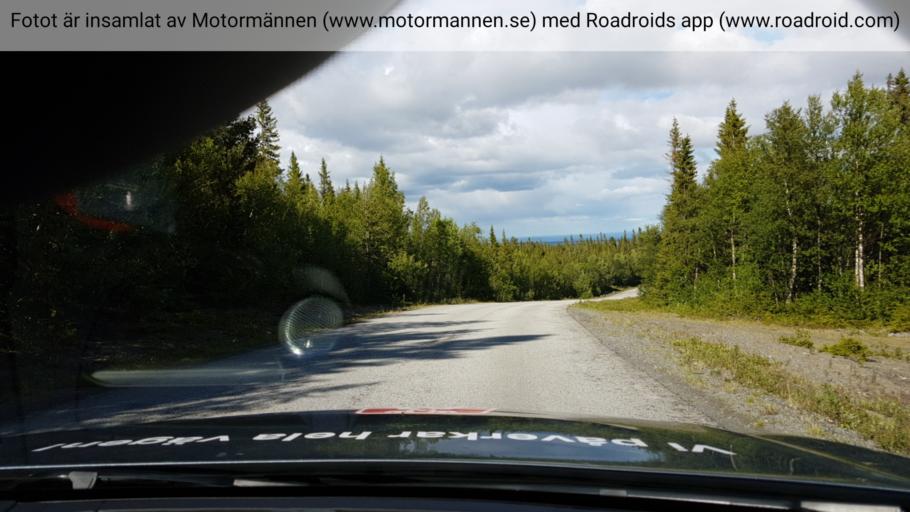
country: SE
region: Jaemtland
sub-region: Krokoms Kommun
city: Valla
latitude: 63.0367
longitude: 13.9544
